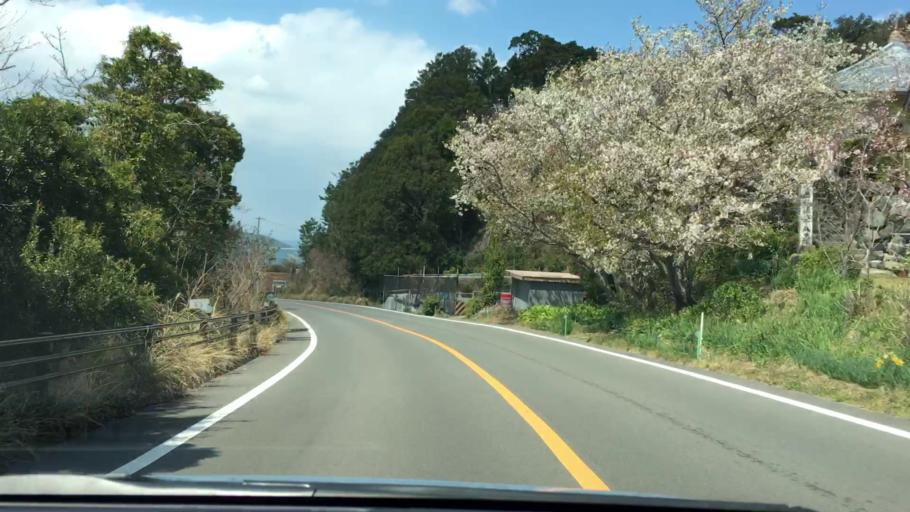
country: JP
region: Mie
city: Toba
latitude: 34.4467
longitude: 136.9147
